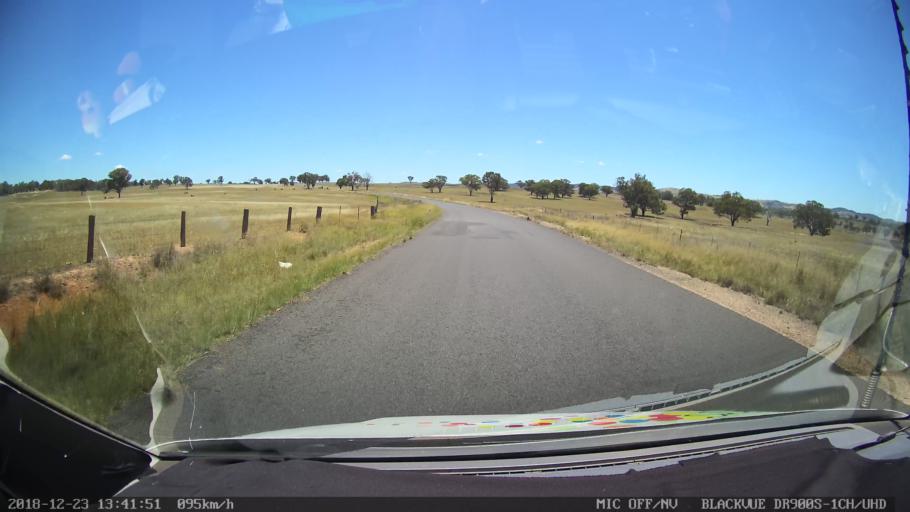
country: AU
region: New South Wales
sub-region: Armidale Dumaresq
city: Armidale
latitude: -30.4710
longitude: 151.1698
